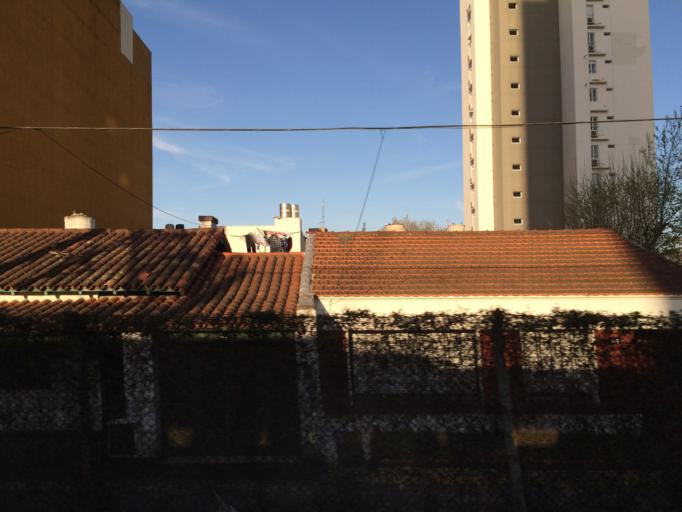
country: AR
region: Buenos Aires
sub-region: Partido de Lomas de Zamora
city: Lomas de Zamora
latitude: -34.7657
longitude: -58.3975
